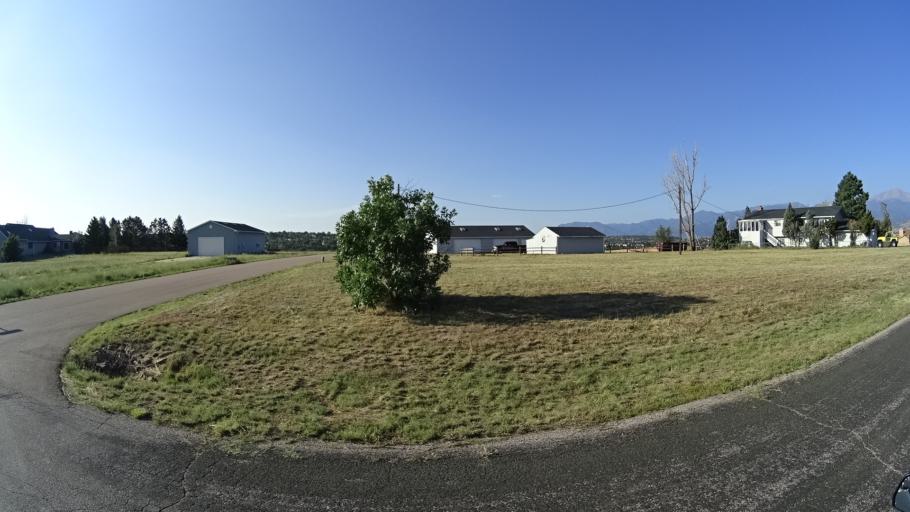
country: US
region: Colorado
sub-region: El Paso County
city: Black Forest
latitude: 38.9367
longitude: -104.7739
